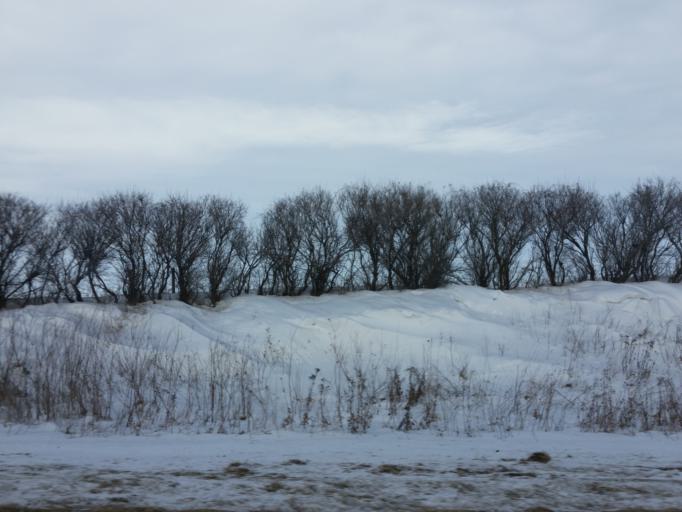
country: US
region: Iowa
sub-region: Delaware County
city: Manchester
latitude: 42.4646
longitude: -91.6239
